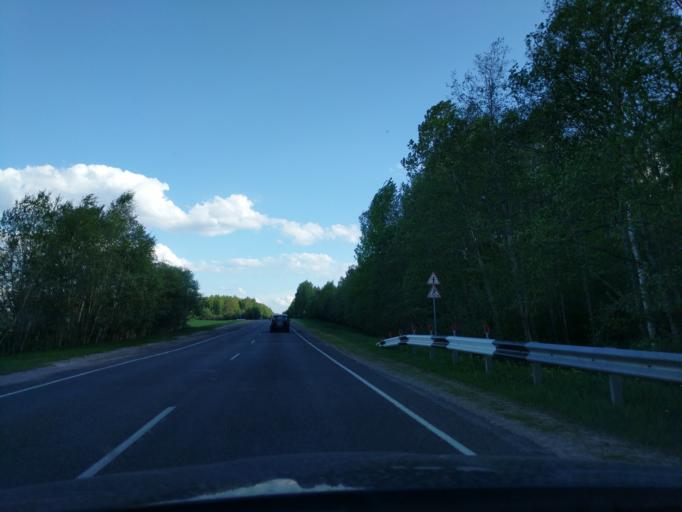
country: BY
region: Minsk
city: Kryvichy
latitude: 54.6082
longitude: 27.1804
